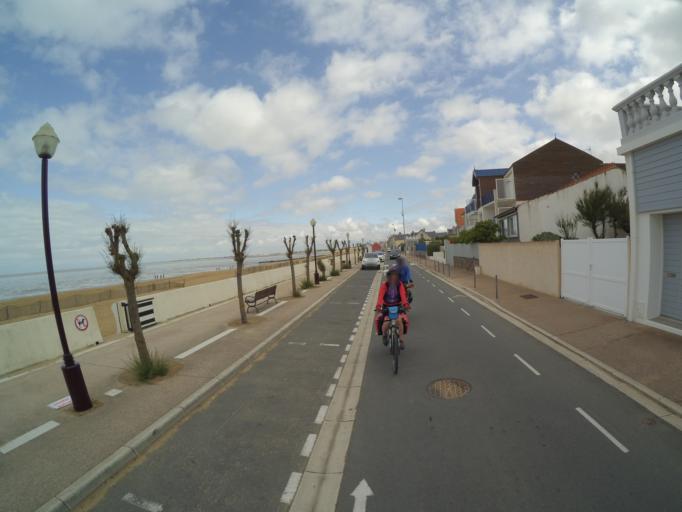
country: FR
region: Poitou-Charentes
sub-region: Departement de la Charente-Maritime
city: Chatelaillon-Plage
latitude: 46.0700
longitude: -1.0929
